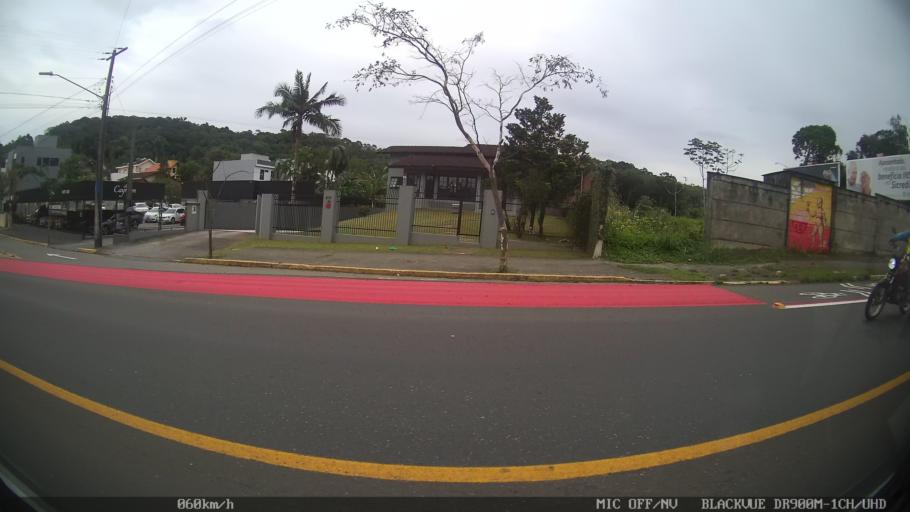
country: BR
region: Santa Catarina
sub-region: Joinville
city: Joinville
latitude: -26.2995
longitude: -48.8646
